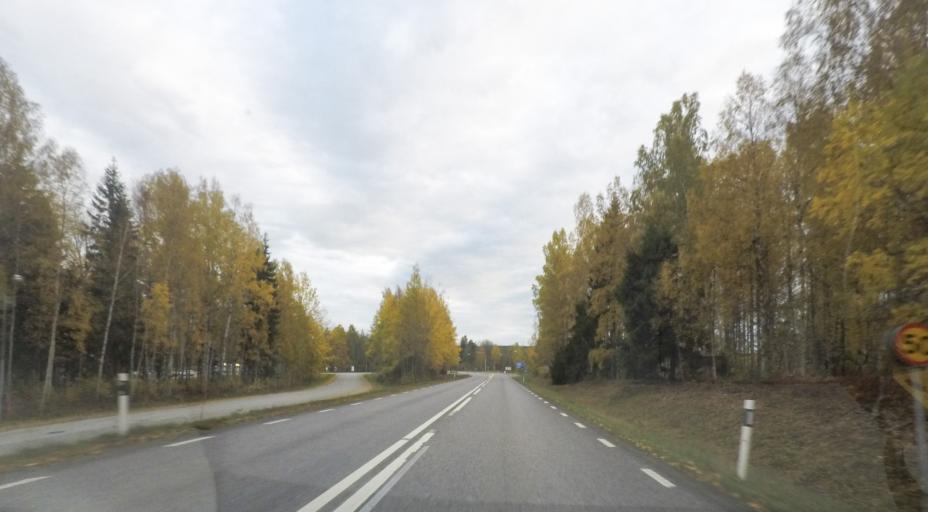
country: SE
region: OErebro
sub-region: Nora Kommun
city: As
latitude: 59.5105
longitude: 14.9645
